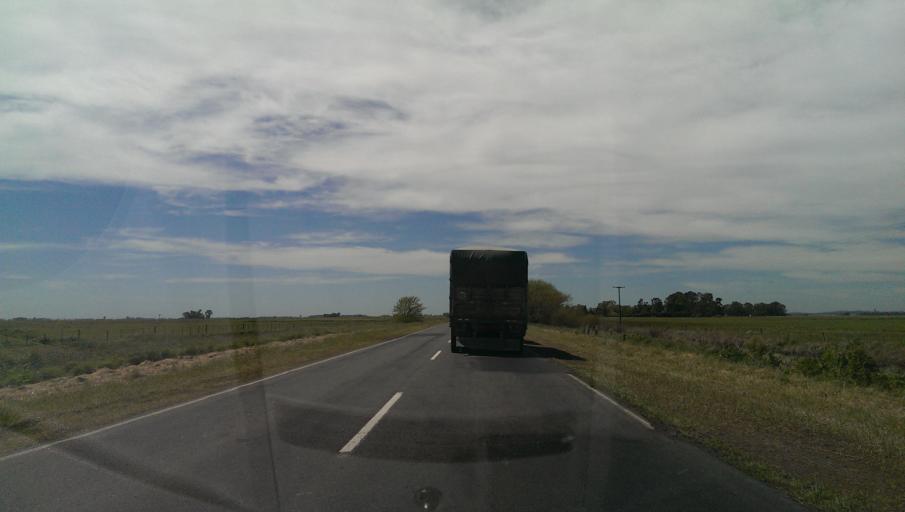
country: AR
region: Buenos Aires
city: Olavarria
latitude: -37.0264
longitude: -60.4191
